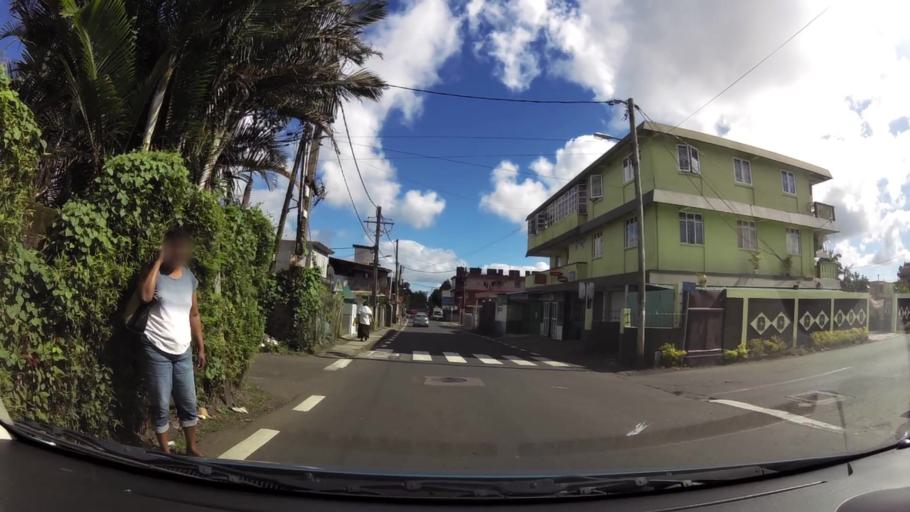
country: MU
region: Plaines Wilhems
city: Curepipe
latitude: -20.3316
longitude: 57.5223
